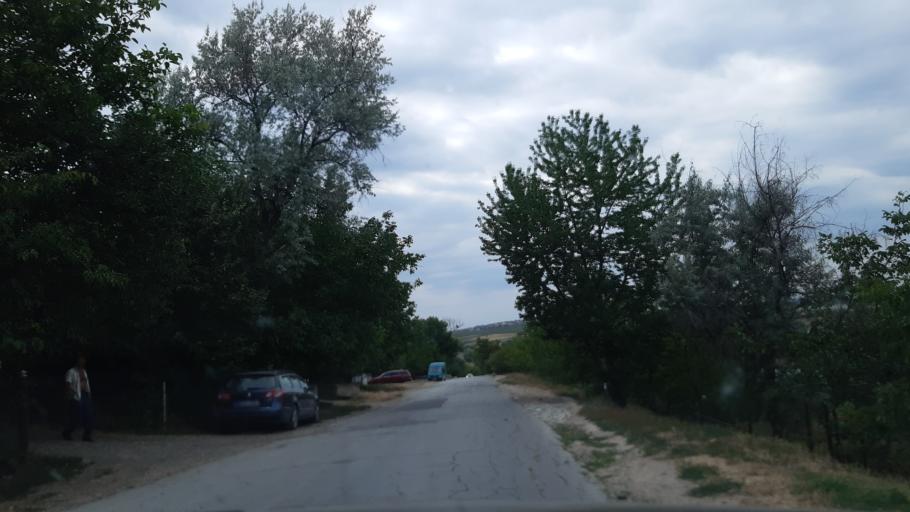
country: MD
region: Chisinau
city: Vatra
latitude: 47.0547
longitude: 28.7301
